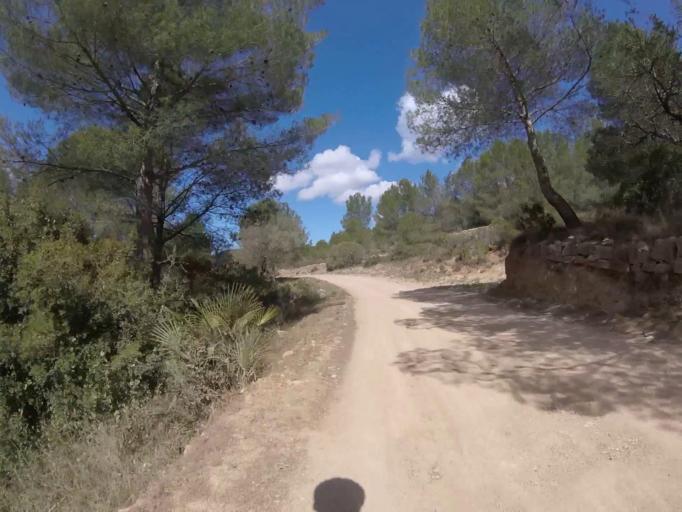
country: ES
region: Valencia
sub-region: Provincia de Castello
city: Santa Magdalena de Pulpis
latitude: 40.3235
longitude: 0.3451
